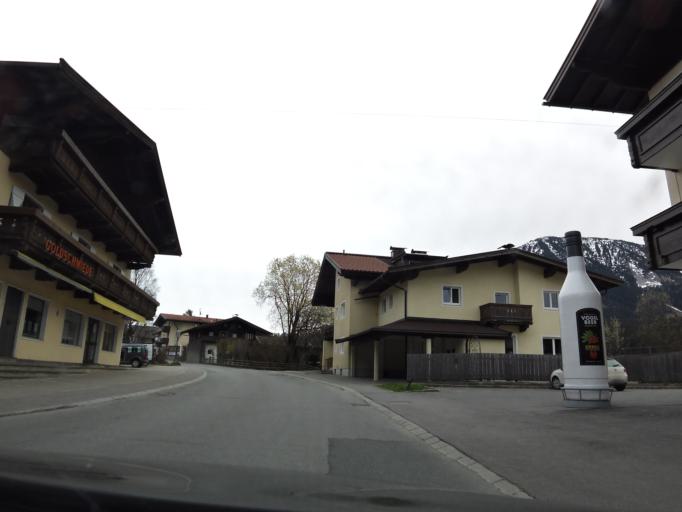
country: AT
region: Tyrol
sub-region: Politischer Bezirk Kitzbuhel
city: Brixen im Thale
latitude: 47.4496
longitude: 12.2562
